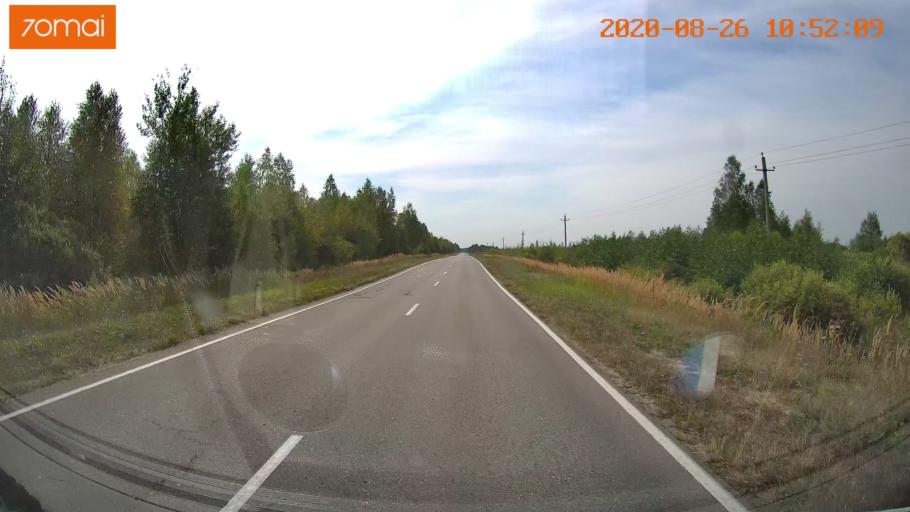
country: RU
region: Rjazan
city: Lashma
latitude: 54.6613
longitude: 41.1539
